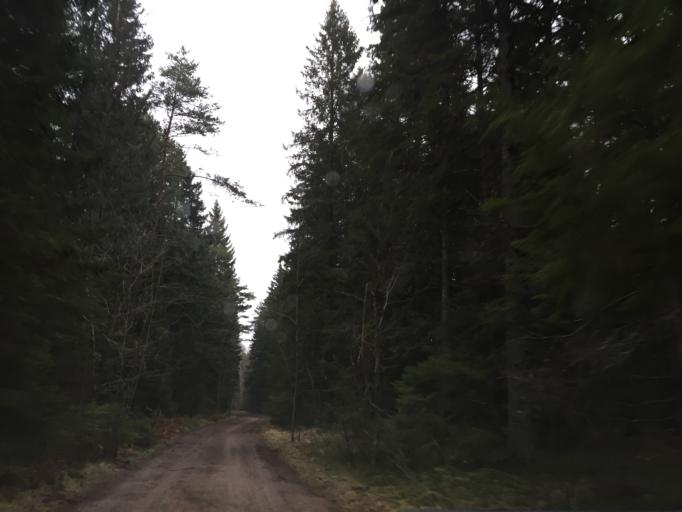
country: EE
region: Saare
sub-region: Kuressaare linn
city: Kuressaare
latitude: 58.4922
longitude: 22.3715
